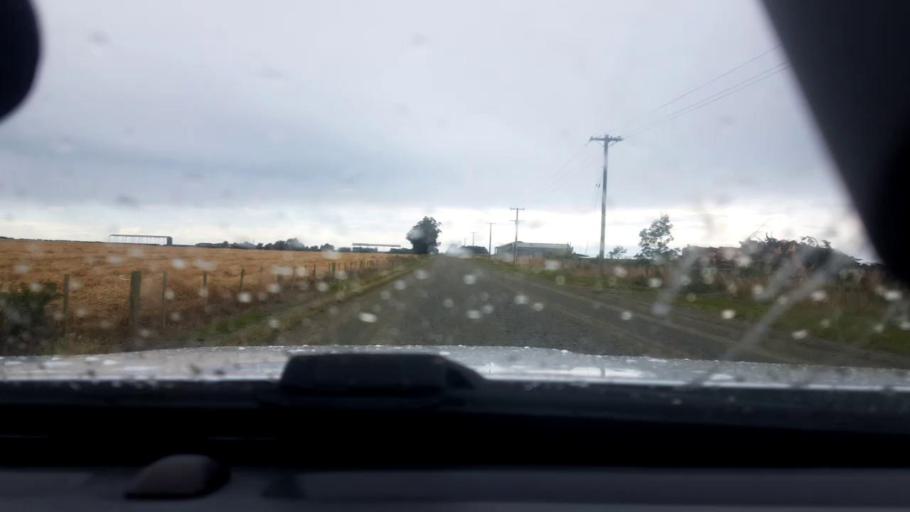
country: NZ
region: Canterbury
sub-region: Timaru District
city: Pleasant Point
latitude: -44.1338
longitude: 171.4080
